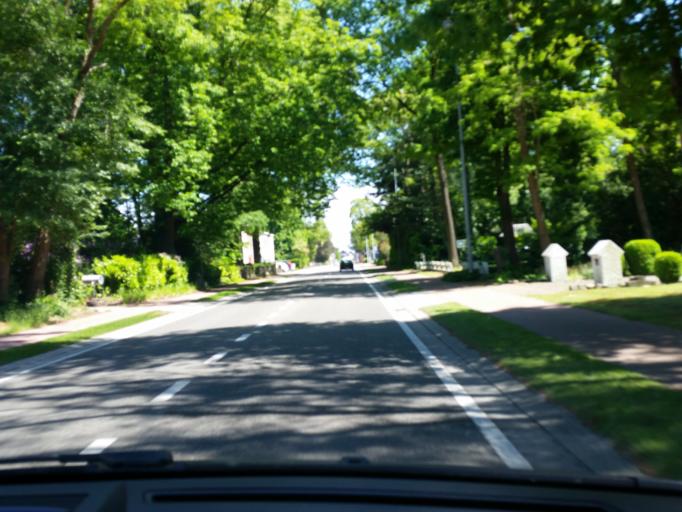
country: BE
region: Flanders
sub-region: Provincie Antwerpen
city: Bonheiden
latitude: 51.0261
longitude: 4.5360
